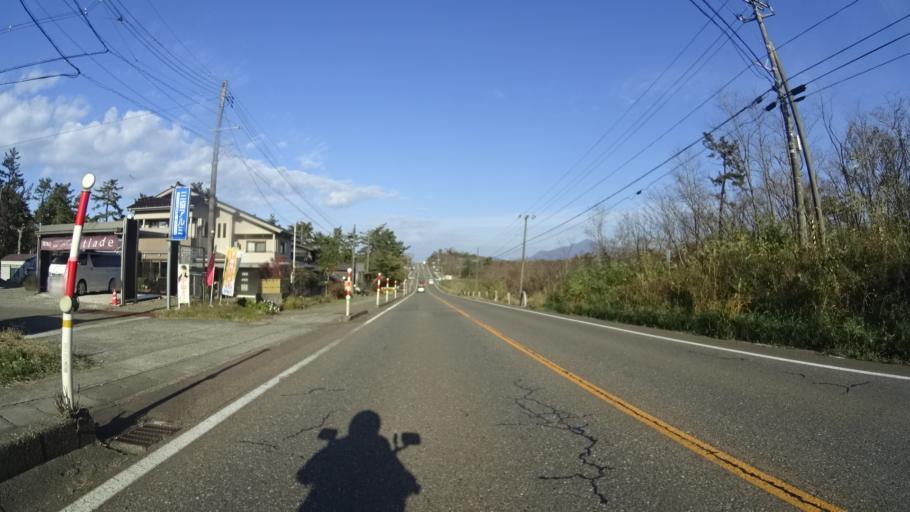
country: JP
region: Niigata
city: Joetsu
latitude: 37.2398
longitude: 138.3445
